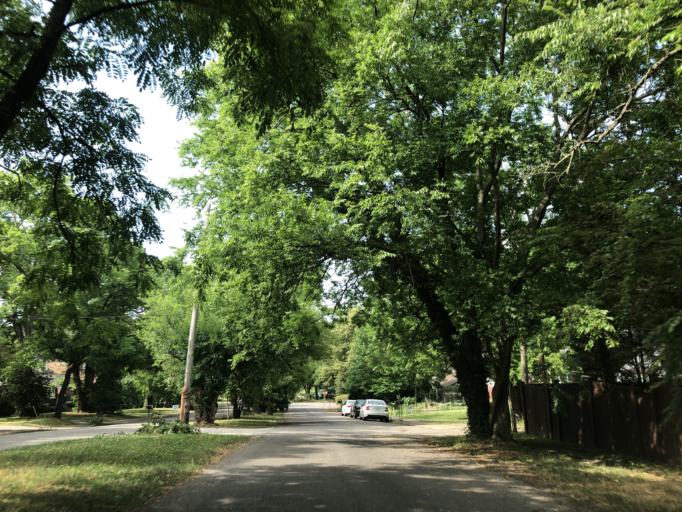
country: US
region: Tennessee
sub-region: Davidson County
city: Oak Hill
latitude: 36.1216
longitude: -86.7977
